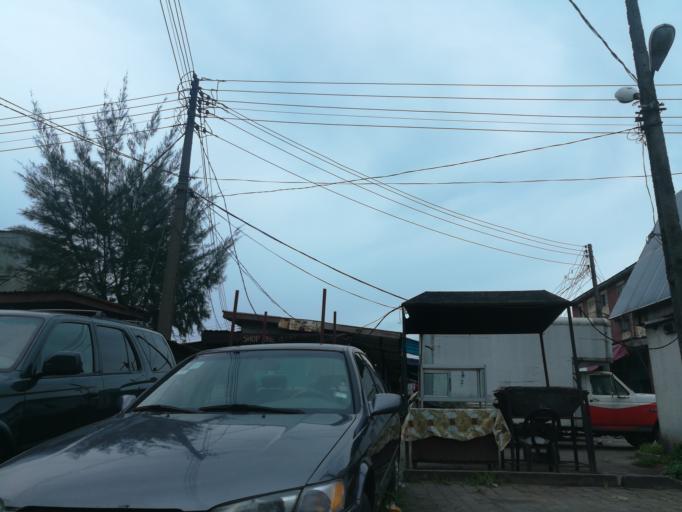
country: NG
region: Lagos
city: Ebute Metta
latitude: 6.4908
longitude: 3.3843
